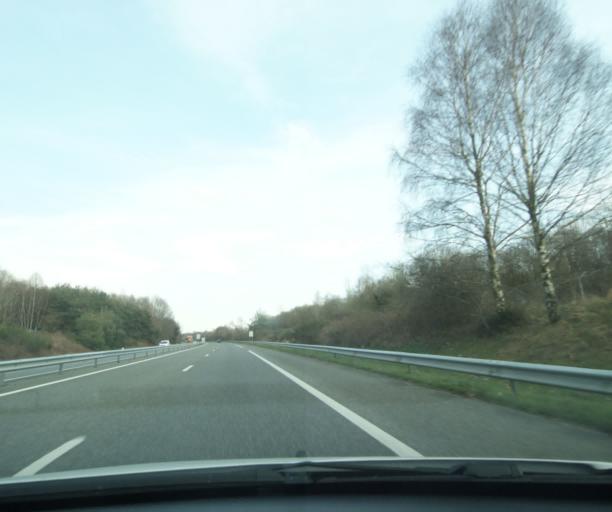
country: FR
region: Midi-Pyrenees
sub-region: Departement des Hautes-Pyrenees
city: La Barthe-de-Neste
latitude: 43.0992
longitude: 0.3970
